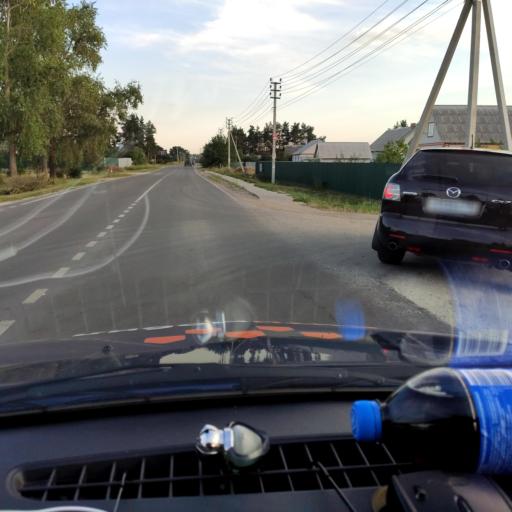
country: RU
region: Voronezj
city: Podgornoye
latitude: 51.8778
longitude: 39.1731
